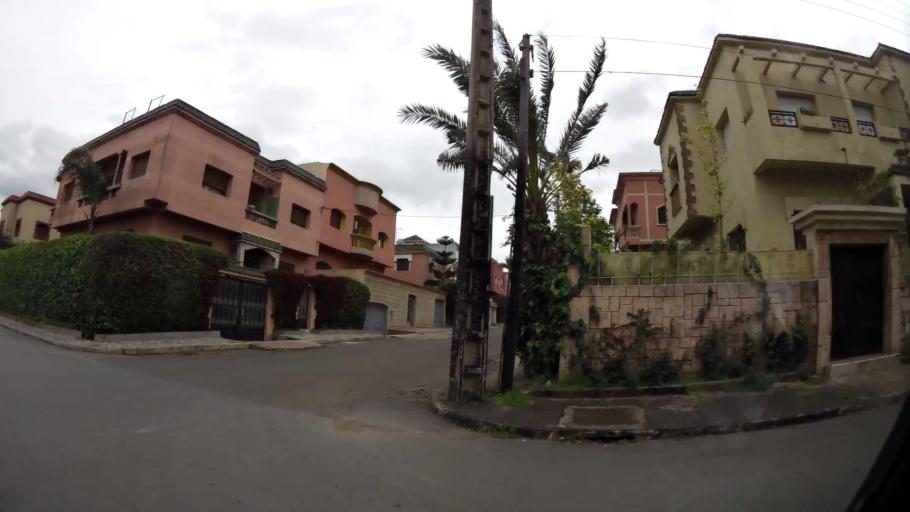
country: MA
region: Grand Casablanca
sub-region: Mediouna
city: Tit Mellil
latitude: 33.5646
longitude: -7.5325
